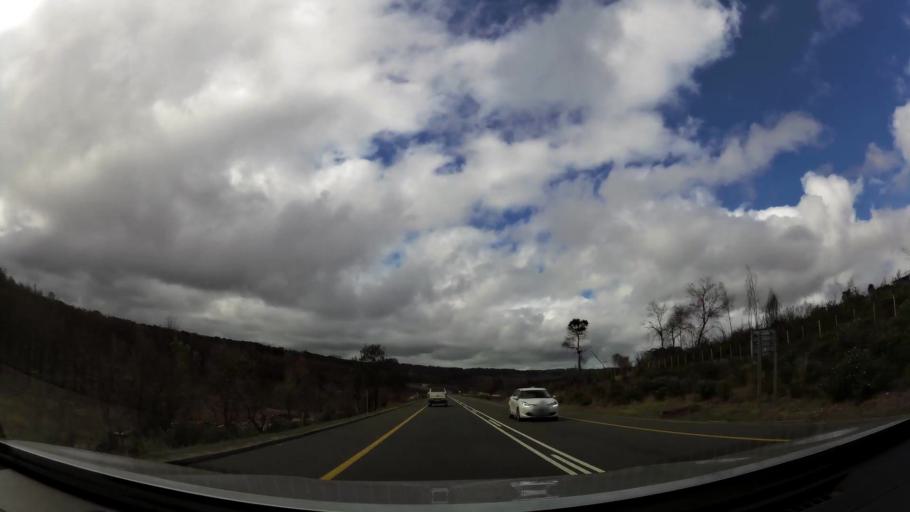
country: ZA
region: Western Cape
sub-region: Eden District Municipality
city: Knysna
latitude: -34.0367
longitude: 23.1501
